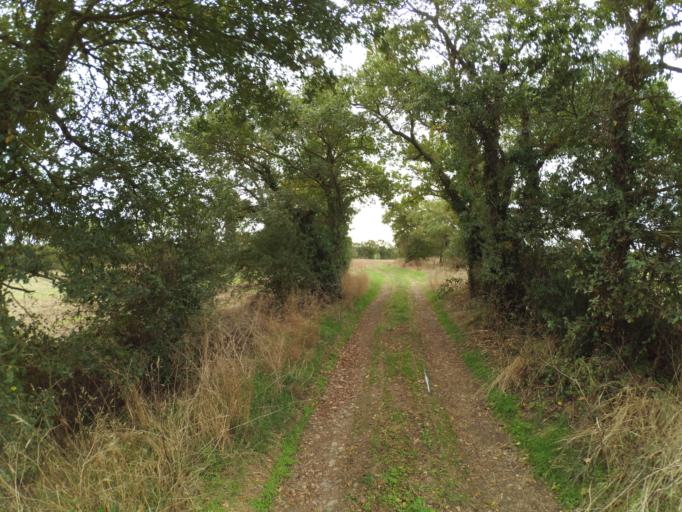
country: FR
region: Pays de la Loire
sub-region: Departement de la Loire-Atlantique
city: Remouille
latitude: 47.0564
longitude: -1.3523
